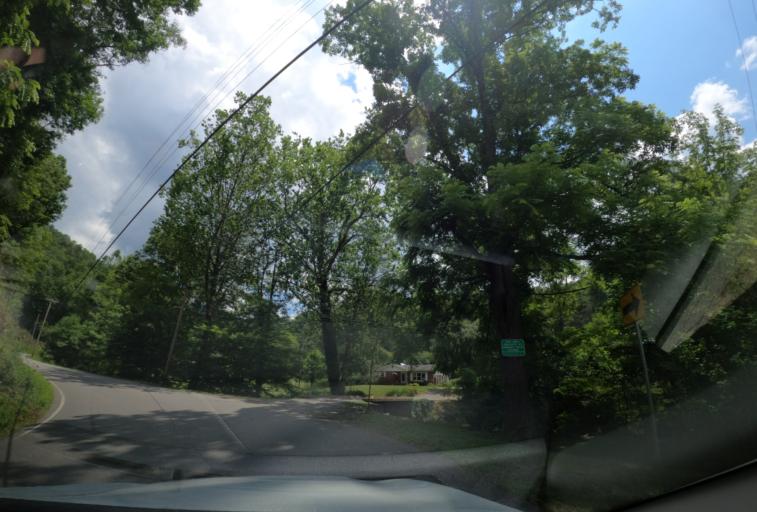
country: US
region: North Carolina
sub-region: Haywood County
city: Waynesville
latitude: 35.4227
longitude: -82.9128
